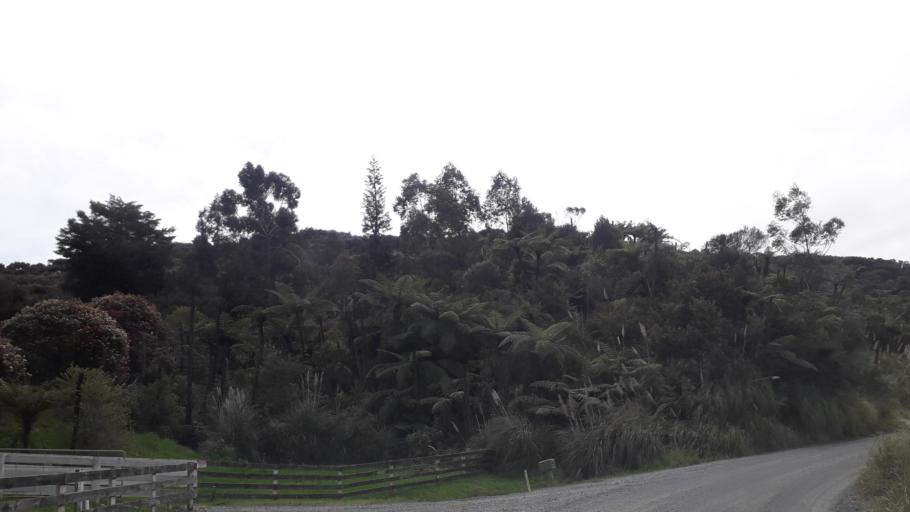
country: NZ
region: Northland
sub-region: Far North District
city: Taipa
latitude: -35.0205
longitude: 173.5499
